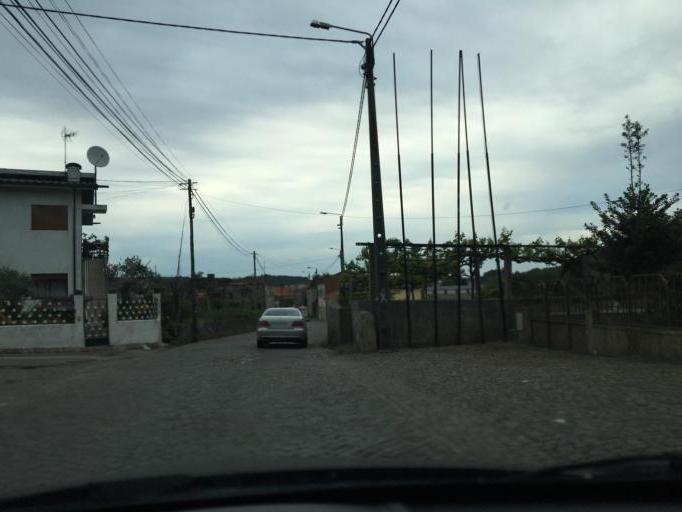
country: PT
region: Porto
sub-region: Maia
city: Anta
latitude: 41.2697
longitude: -8.6186
